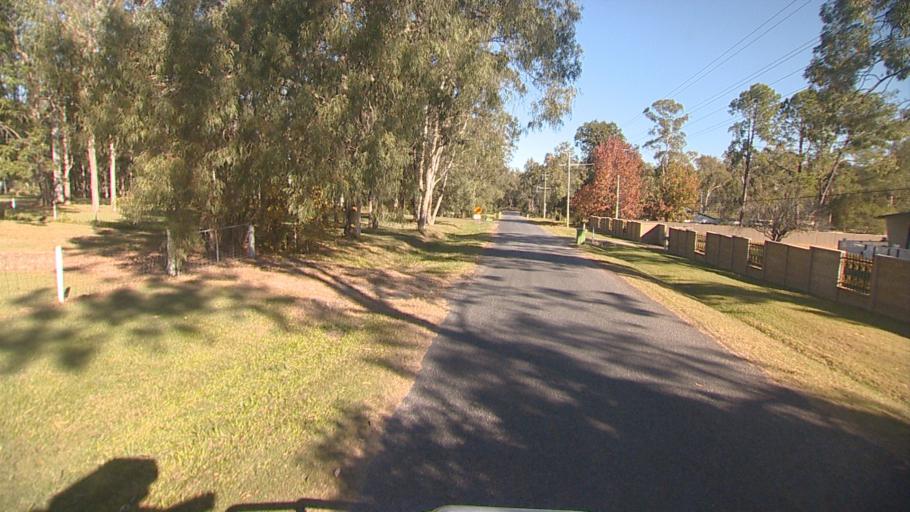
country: AU
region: Queensland
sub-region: Logan
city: Park Ridge South
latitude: -27.7307
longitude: 153.0114
